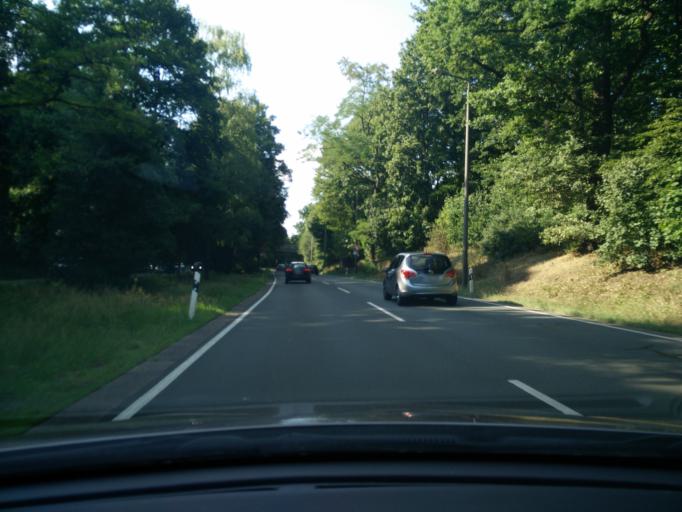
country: DE
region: Bavaria
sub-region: Regierungsbezirk Mittelfranken
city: Nuernberg
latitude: 49.4334
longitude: 11.1028
